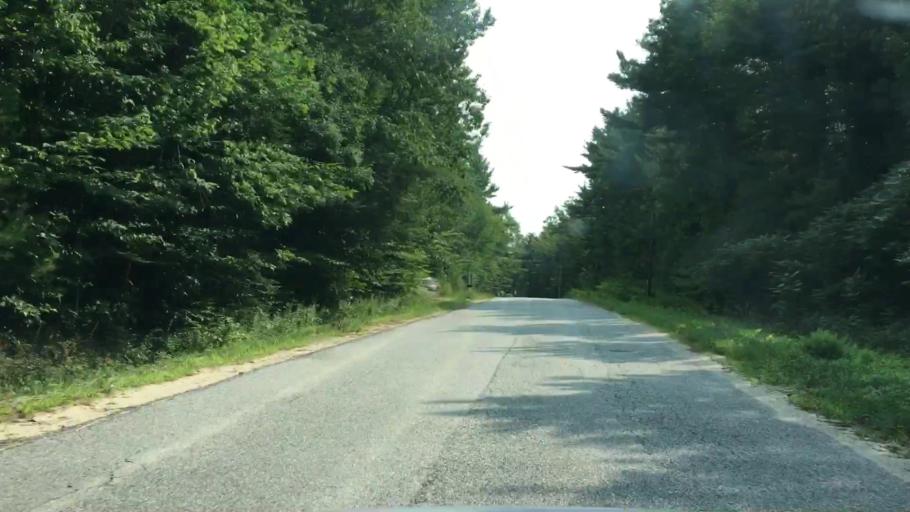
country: US
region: Maine
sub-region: Androscoggin County
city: Livermore
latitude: 44.3242
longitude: -70.2899
